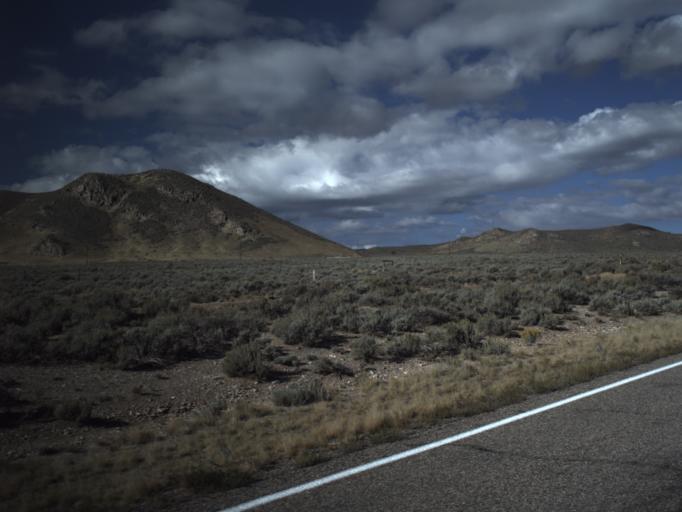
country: US
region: Utah
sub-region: Beaver County
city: Milford
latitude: 38.4189
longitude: -113.0930
